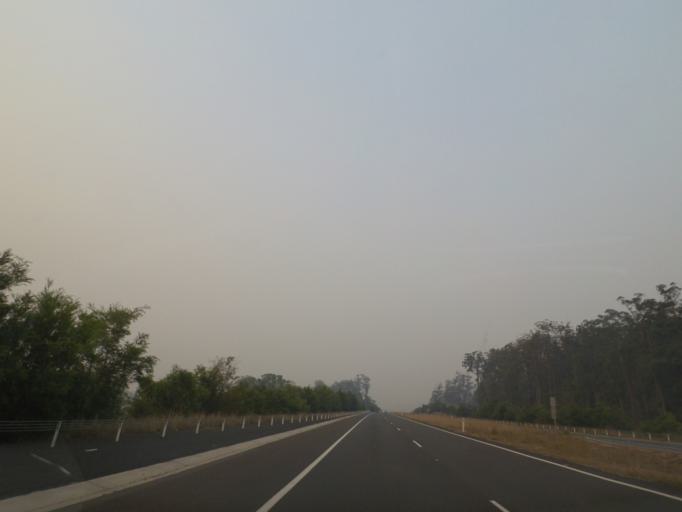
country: AU
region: New South Wales
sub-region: Nambucca Shire
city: Macksville
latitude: -30.7759
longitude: 152.8958
